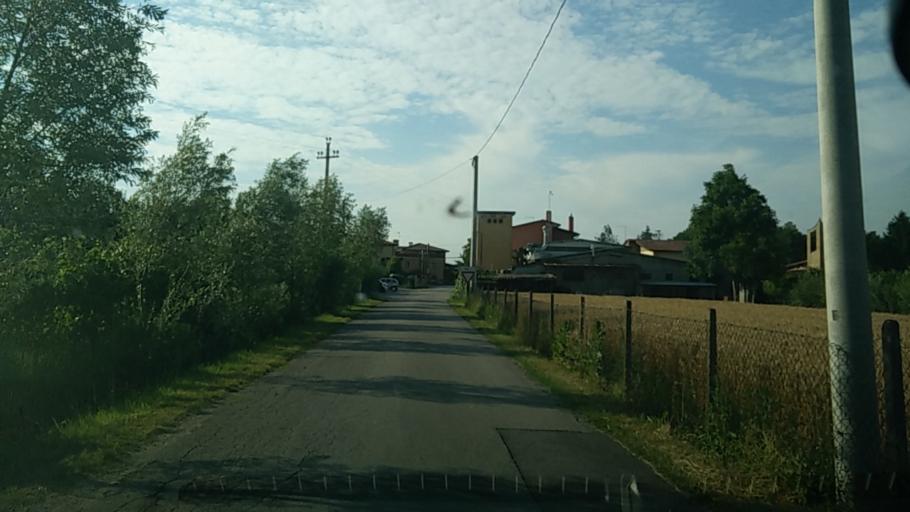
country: IT
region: Veneto
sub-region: Provincia di Venezia
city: Musile di Piave
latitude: 45.6035
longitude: 12.5354
